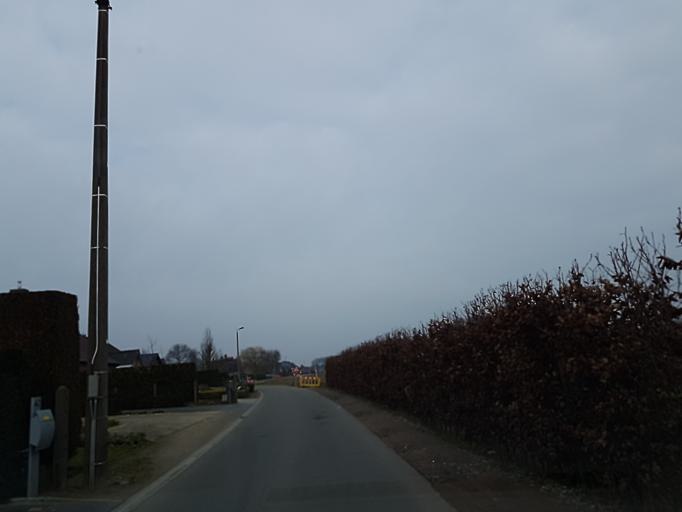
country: BE
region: Flanders
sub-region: Provincie Oost-Vlaanderen
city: Nevele
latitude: 51.0256
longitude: 3.5445
